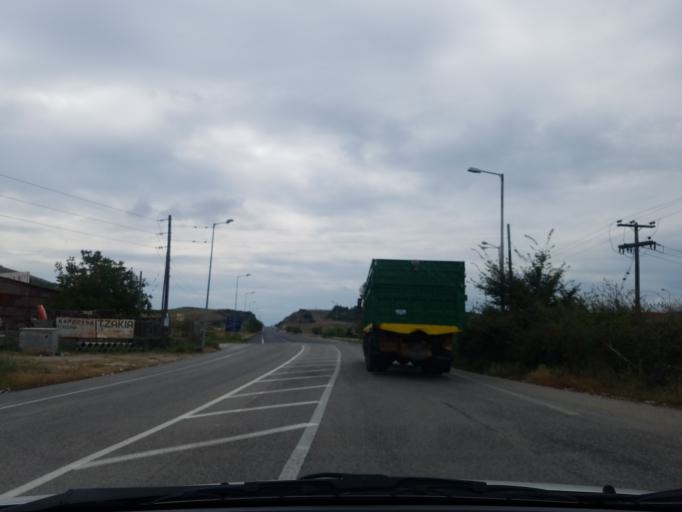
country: GR
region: Central Greece
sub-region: Nomos Fthiotidos
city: Domokos
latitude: 39.1119
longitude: 22.3082
